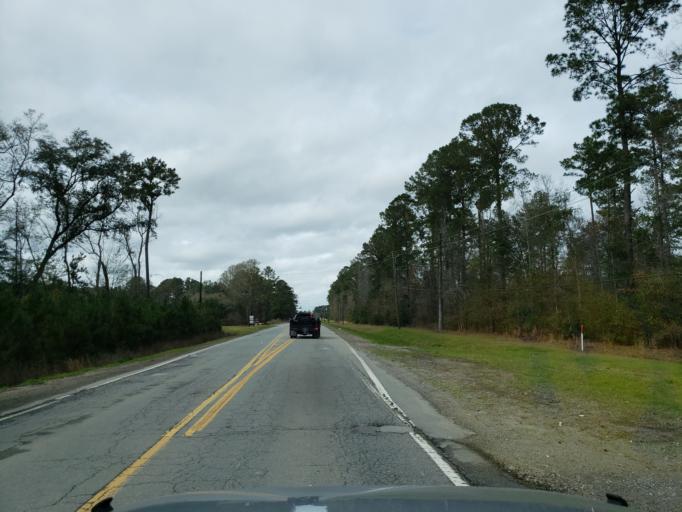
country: US
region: Georgia
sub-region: Chatham County
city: Georgetown
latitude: 32.0144
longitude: -81.2588
